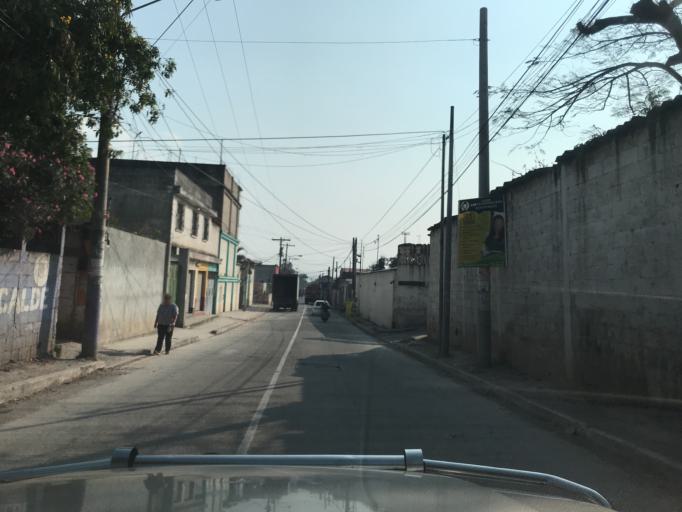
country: GT
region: Guatemala
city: Santa Catarina Pinula
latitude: 14.5559
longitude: -90.5252
